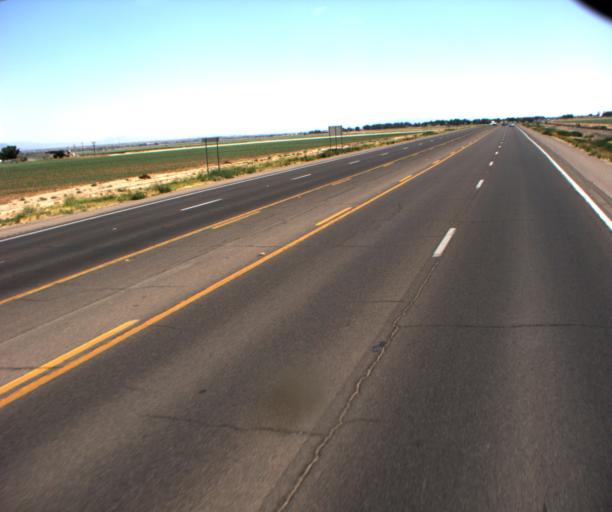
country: US
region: Arizona
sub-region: Graham County
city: Pima
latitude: 32.8861
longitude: -109.8135
